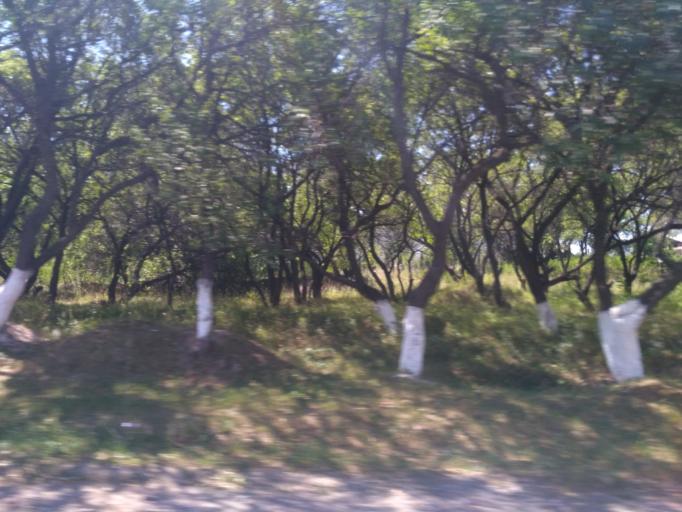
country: KZ
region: Almaty Oblysy
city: Burunday
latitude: 43.1664
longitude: 76.5842
